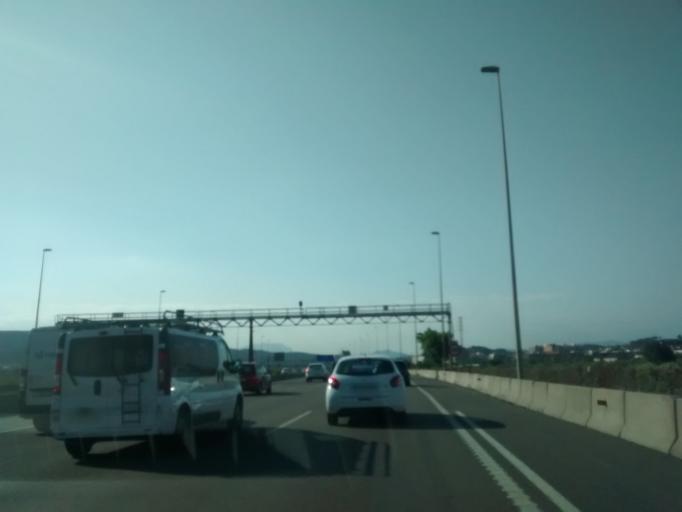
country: ES
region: Catalonia
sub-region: Provincia de Barcelona
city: Sant Vicenc dels Horts
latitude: 41.3976
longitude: 2.0225
